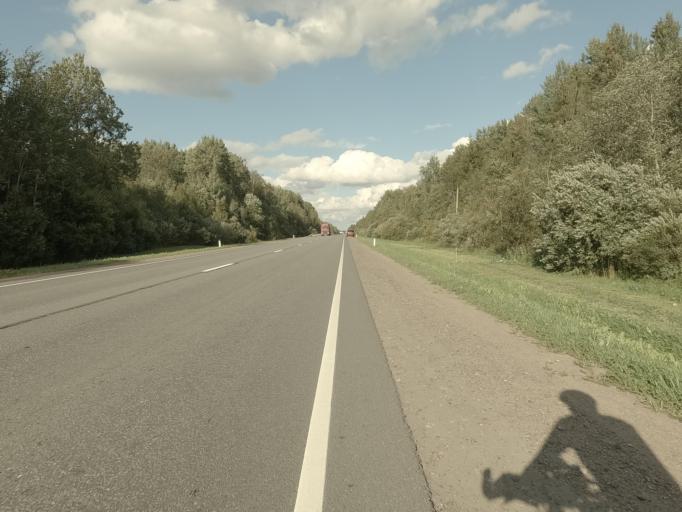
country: RU
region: Leningrad
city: Nikol'skoye
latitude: 59.6498
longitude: 30.8496
